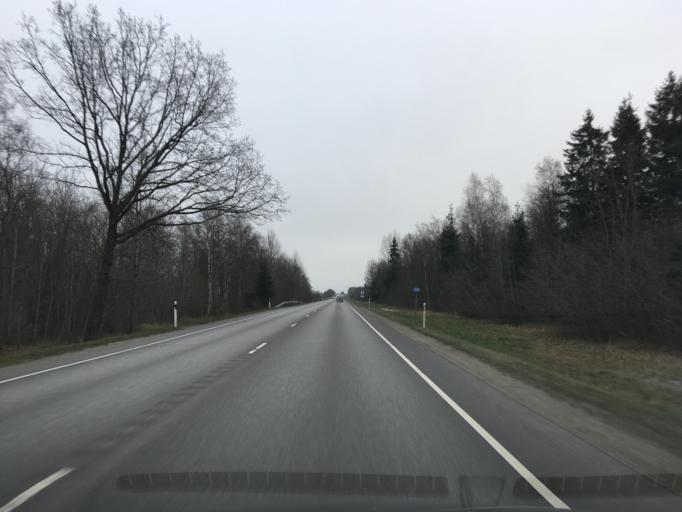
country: EE
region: Ida-Virumaa
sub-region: Kohtla-Jaerve linn
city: Kohtla-Jarve
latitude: 59.4162
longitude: 27.2932
